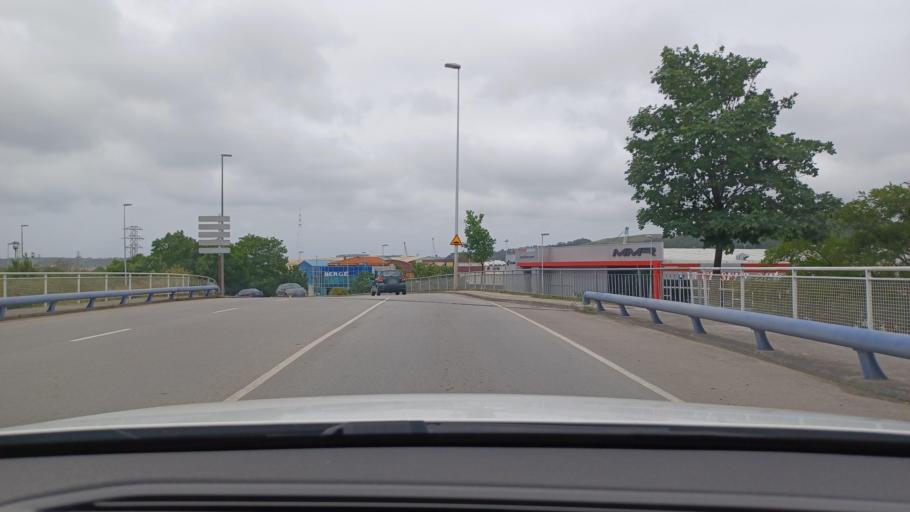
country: ES
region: Asturias
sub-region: Province of Asturias
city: Aviles
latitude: 43.5653
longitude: -5.9255
